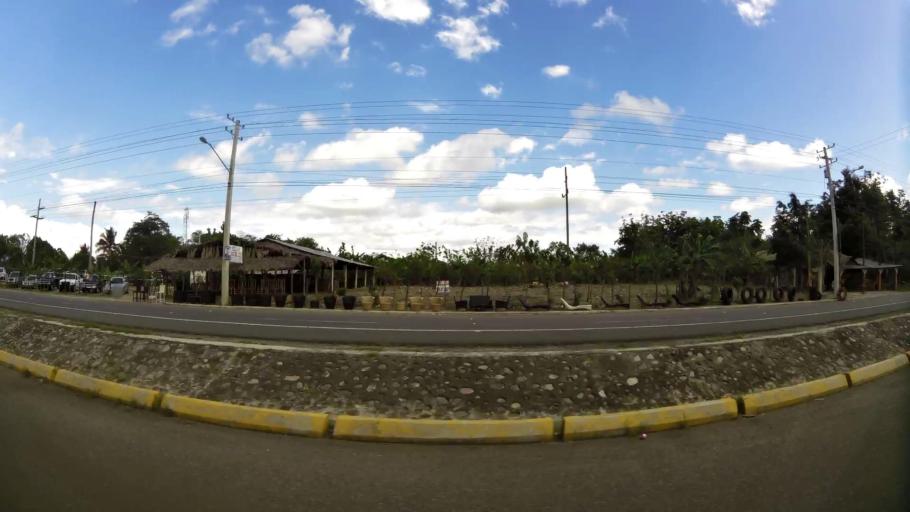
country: DO
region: La Vega
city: Rio Verde Arriba
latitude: 19.3462
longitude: -70.6001
